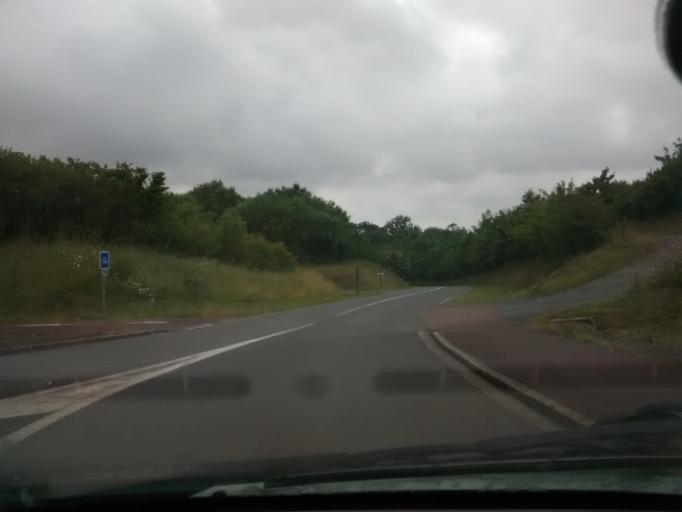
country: FR
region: Lower Normandy
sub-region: Departement de la Manche
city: Saint-Lo
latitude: 49.0977
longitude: -1.0768
